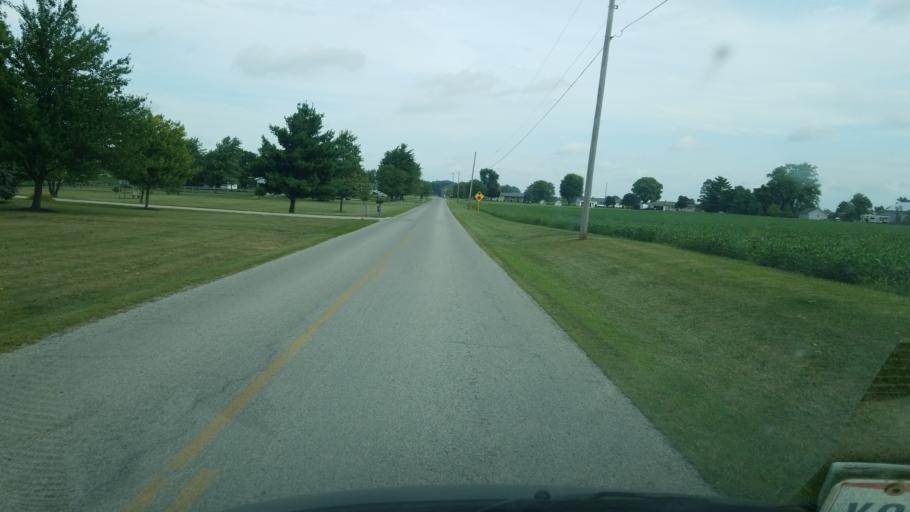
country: US
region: Ohio
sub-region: Seneca County
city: Tiffin
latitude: 41.1071
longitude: -83.0930
